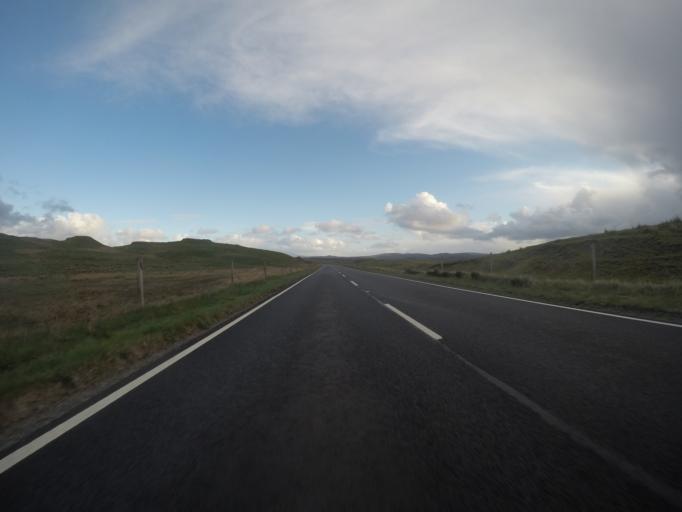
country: GB
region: Scotland
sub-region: Highland
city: Portree
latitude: 57.5442
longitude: -6.3652
